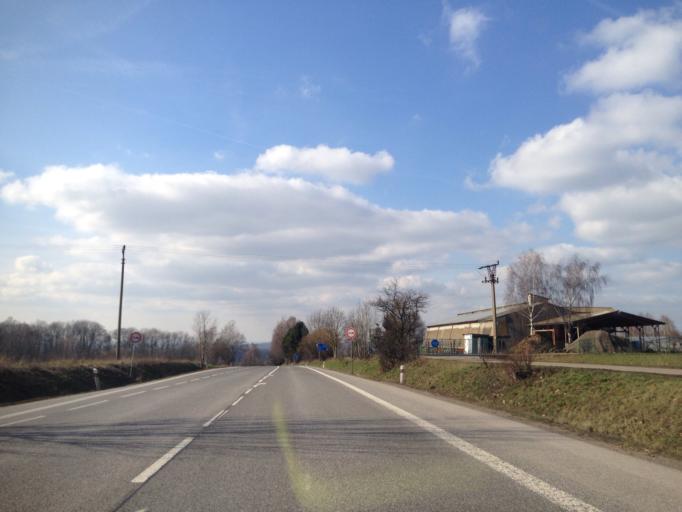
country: CZ
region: Kralovehradecky
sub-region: Okres Jicin
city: Sobotka
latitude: 50.4621
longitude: 15.2036
